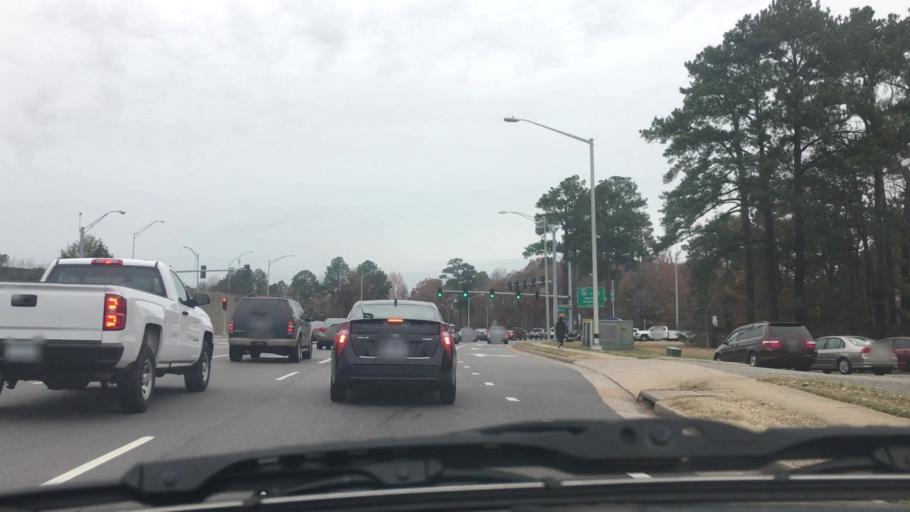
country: US
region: Virginia
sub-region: City of Chesapeake
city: Chesapeake
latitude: 36.8302
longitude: -76.1366
